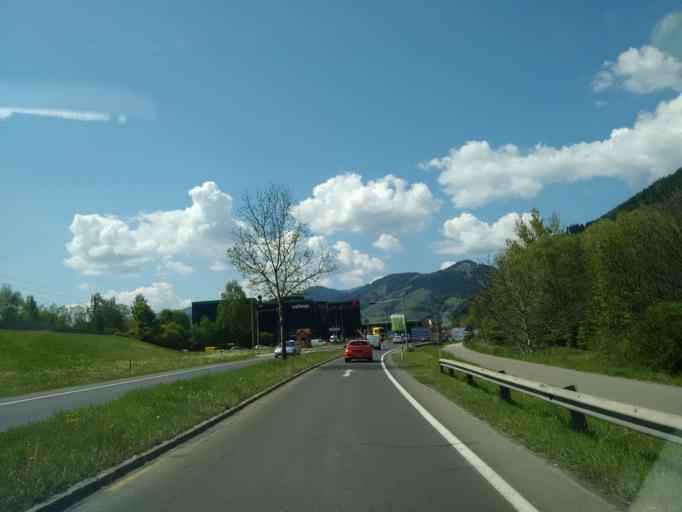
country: AT
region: Styria
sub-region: Politischer Bezirk Bruck-Muerzzuschlag
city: Oberaich
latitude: 47.4004
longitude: 15.2319
